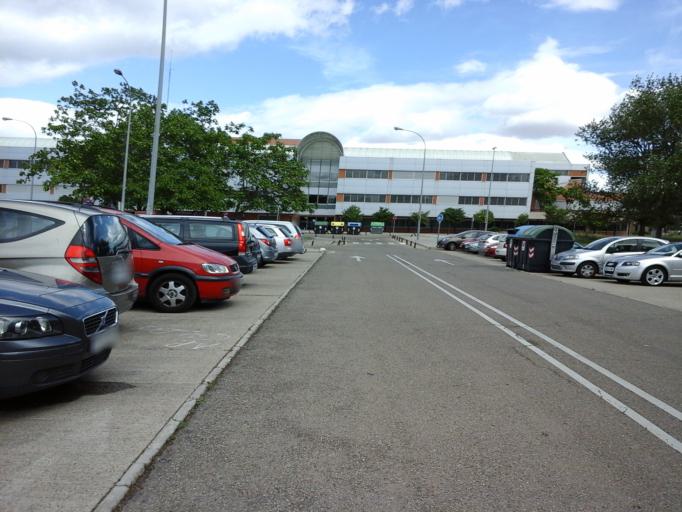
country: ES
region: Aragon
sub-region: Provincia de Zaragoza
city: Almozara
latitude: 41.6822
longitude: -0.8871
